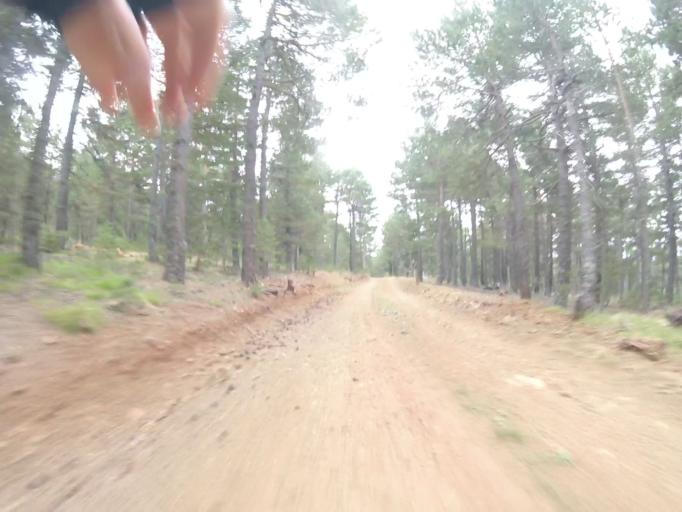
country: ES
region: Aragon
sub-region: Provincia de Teruel
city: Valdelinares
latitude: 40.3694
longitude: -0.6199
